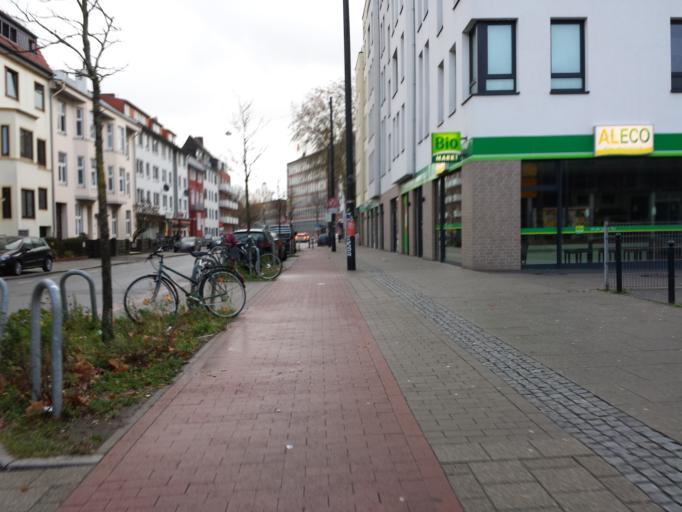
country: DE
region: Bremen
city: Bremen
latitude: 53.0893
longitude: 8.8073
